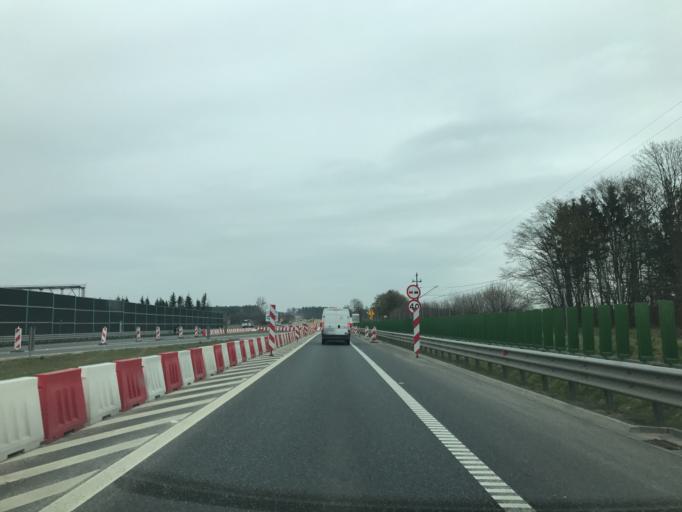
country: PL
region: Warmian-Masurian Voivodeship
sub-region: Powiat olsztynski
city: Olsztynek
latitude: 53.6072
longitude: 20.3185
